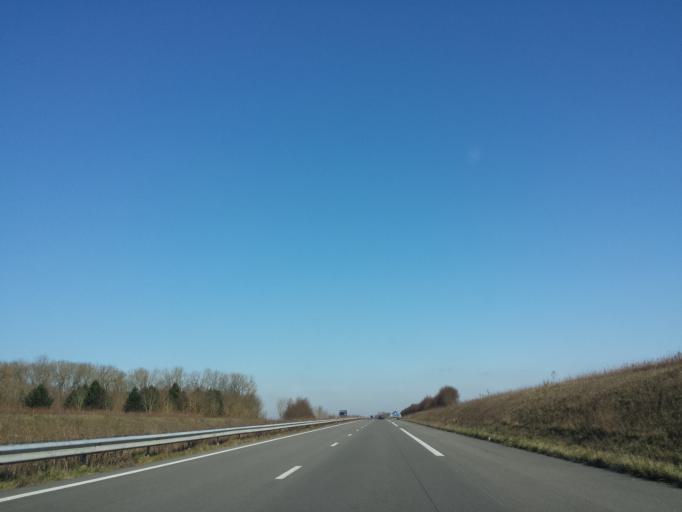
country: FR
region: Picardie
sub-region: Departement de l'Oise
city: Breteuil
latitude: 49.6985
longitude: 2.2339
